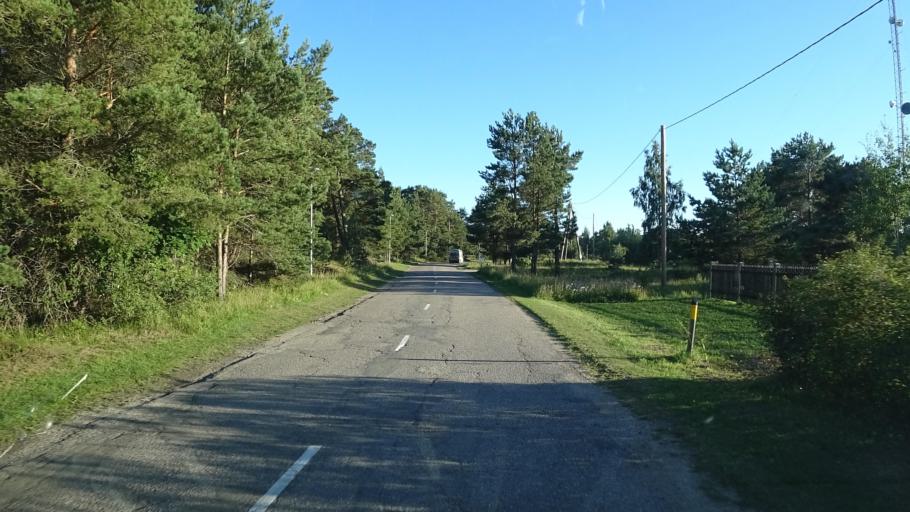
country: LV
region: Rojas
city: Roja
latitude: 57.7483
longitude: 22.5927
